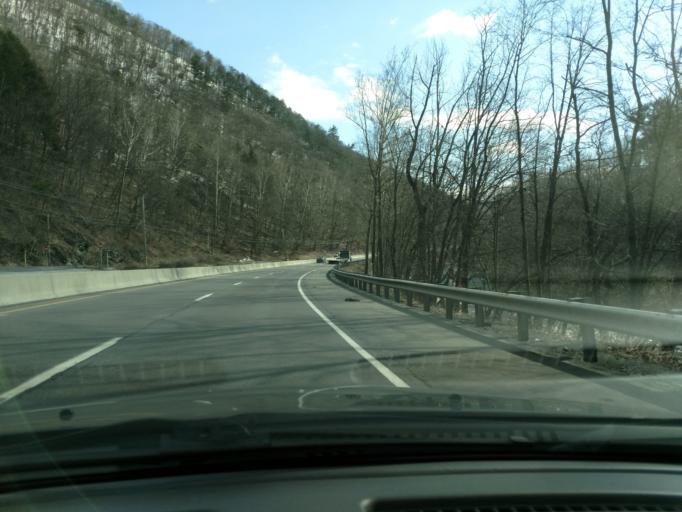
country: US
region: Pennsylvania
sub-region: Berks County
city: West Hamburg
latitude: 40.5999
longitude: -76.0249
